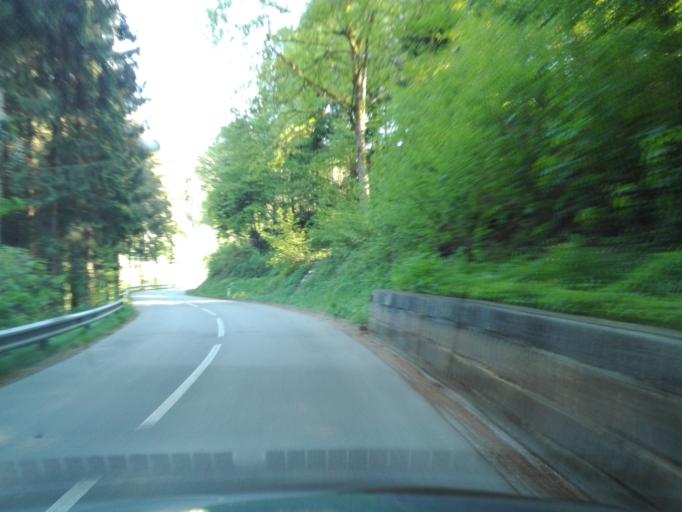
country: DE
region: Bavaria
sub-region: Lower Bavaria
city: Obernzell
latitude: 48.5331
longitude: 13.6484
